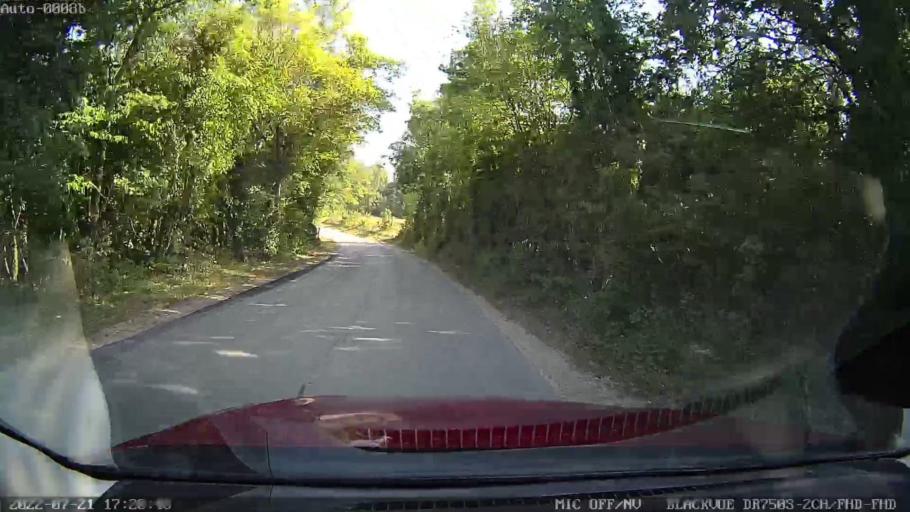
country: HR
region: Istarska
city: Karojba
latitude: 45.2005
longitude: 13.8289
